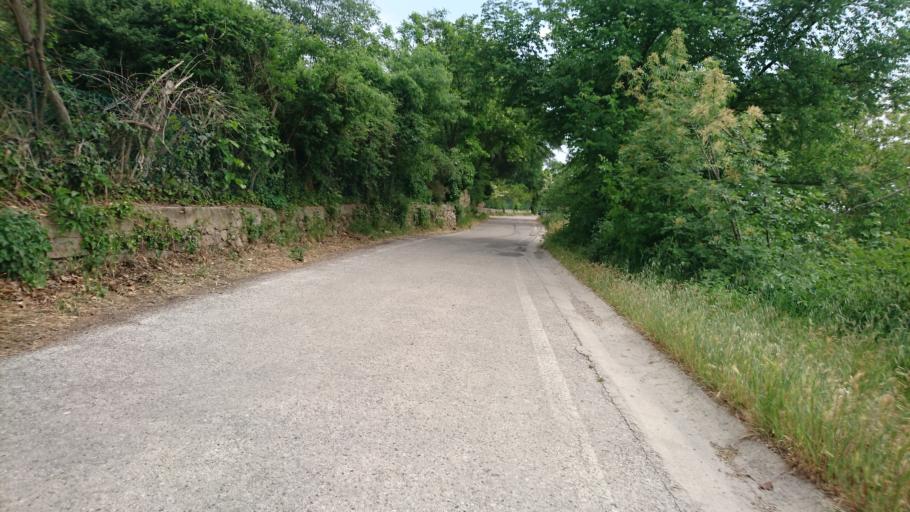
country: IT
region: Veneto
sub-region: Provincia di Padova
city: Monselice
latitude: 45.2490
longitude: 11.7348
